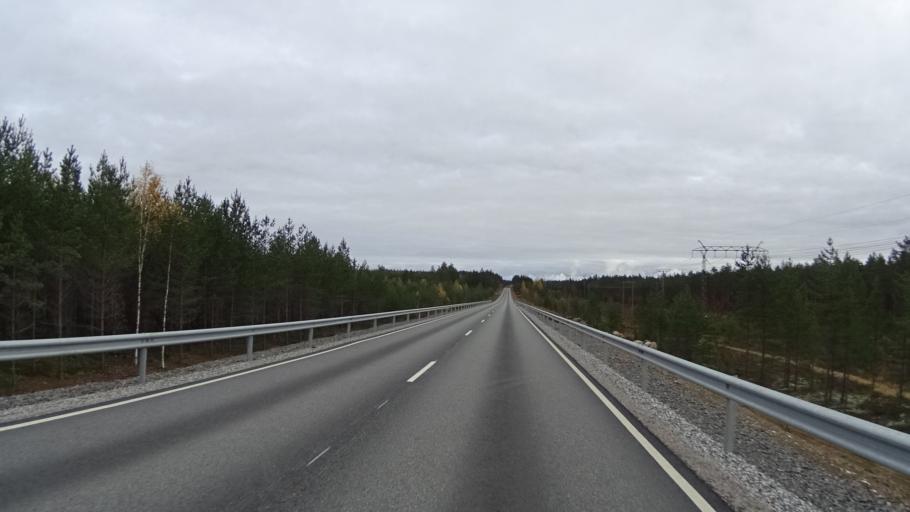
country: FI
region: South Karelia
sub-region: Lappeenranta
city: Lemi
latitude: 60.9807
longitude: 27.8977
